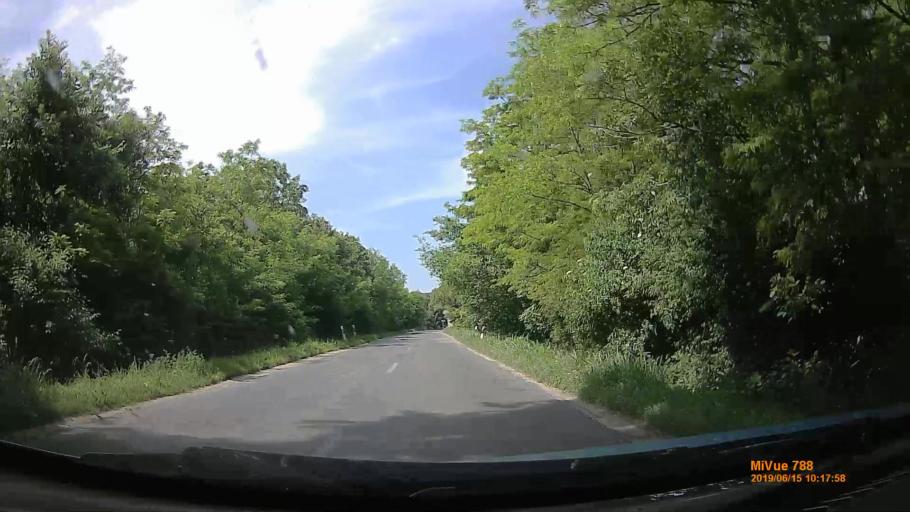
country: HU
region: Baranya
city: Buekkoesd
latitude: 46.1213
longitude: 17.9995
